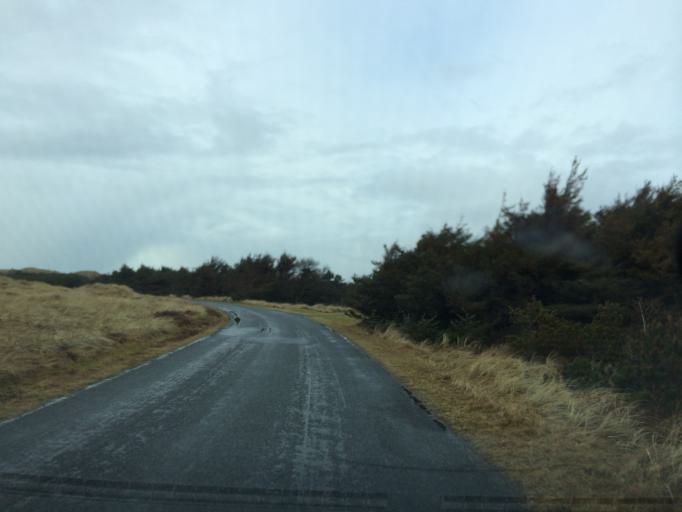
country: DK
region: Central Jutland
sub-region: Holstebro Kommune
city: Ulfborg
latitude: 56.2475
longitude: 8.1384
